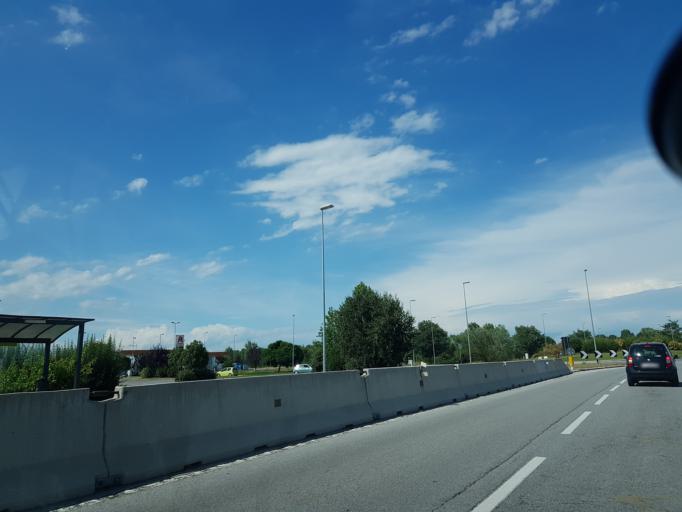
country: IT
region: Piedmont
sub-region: Provincia di Cuneo
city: Cuneo
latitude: 44.3924
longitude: 7.5856
